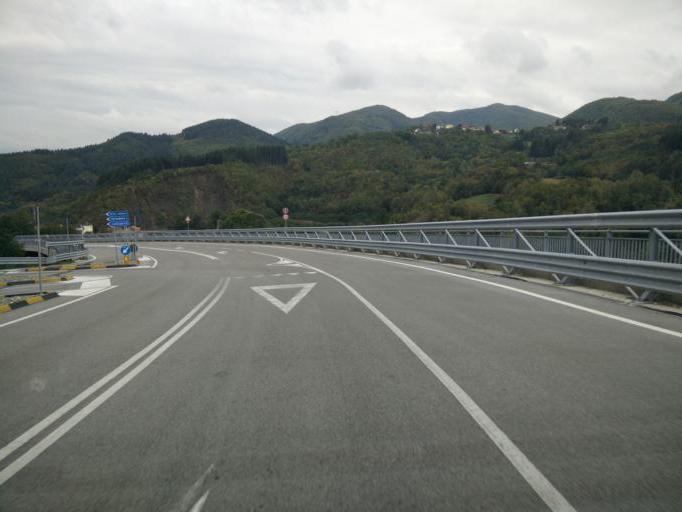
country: IT
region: Tuscany
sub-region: Provincia di Lucca
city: Piazza al Serchio-San Michele
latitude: 44.1783
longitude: 10.3100
